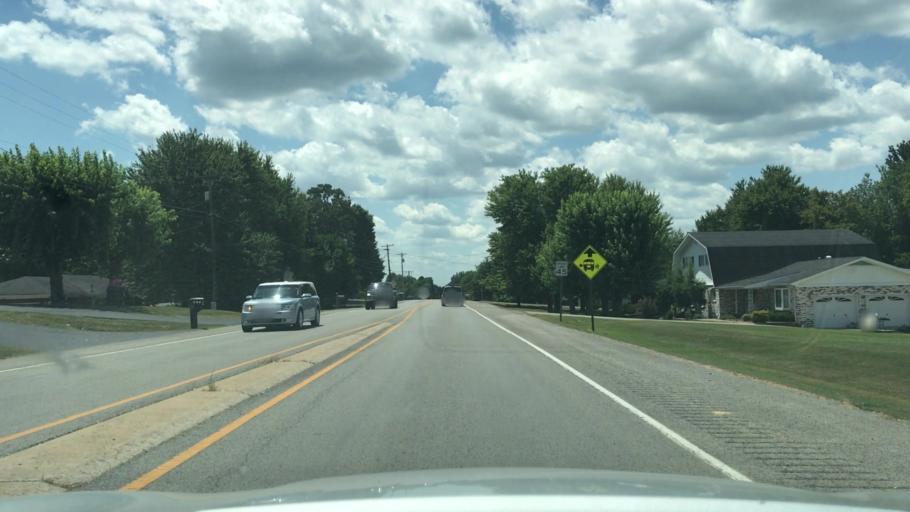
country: US
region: Kentucky
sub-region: Muhlenberg County
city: Greenville
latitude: 37.1995
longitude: -87.2063
